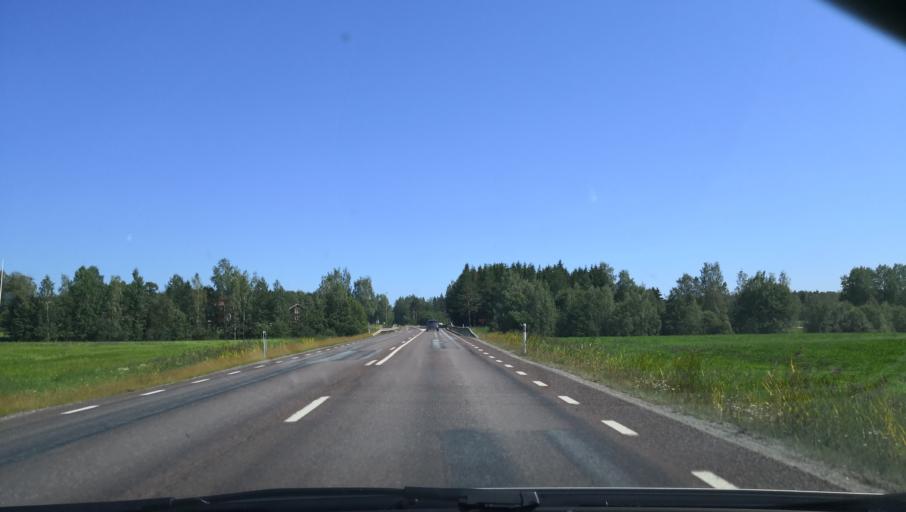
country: SE
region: Gaevleborg
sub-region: Ovanakers Kommun
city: Alfta
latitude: 61.3446
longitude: 16.0820
